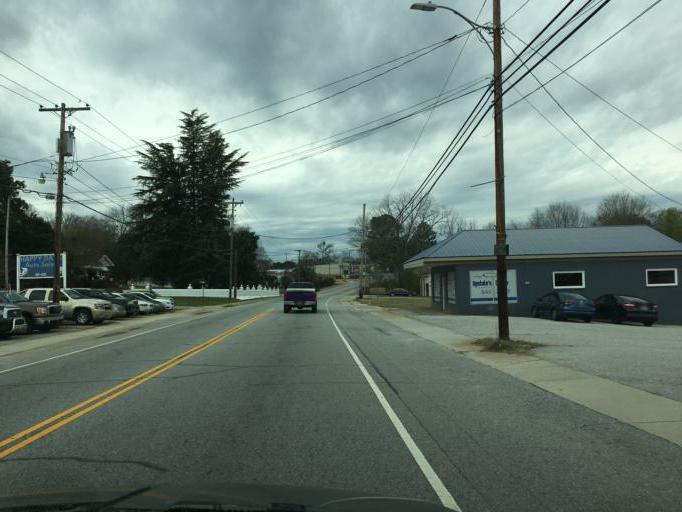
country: US
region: South Carolina
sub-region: Anderson County
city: Piedmont
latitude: 34.7004
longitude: -82.4720
